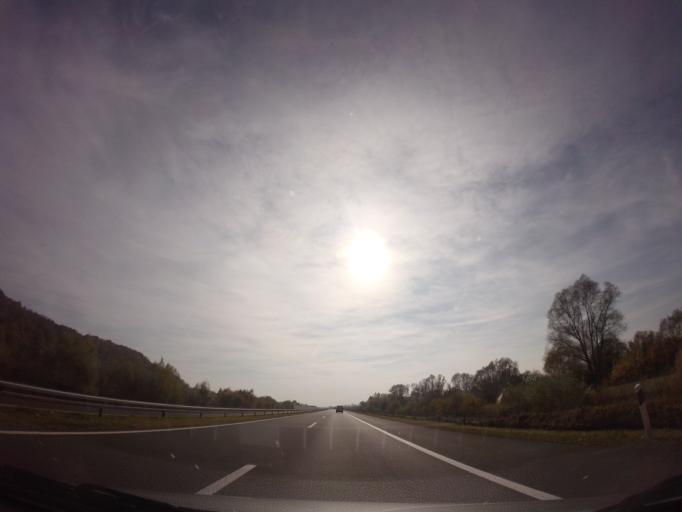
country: HR
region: Varazdinska
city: Remetinec
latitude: 46.0614
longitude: 16.2981
